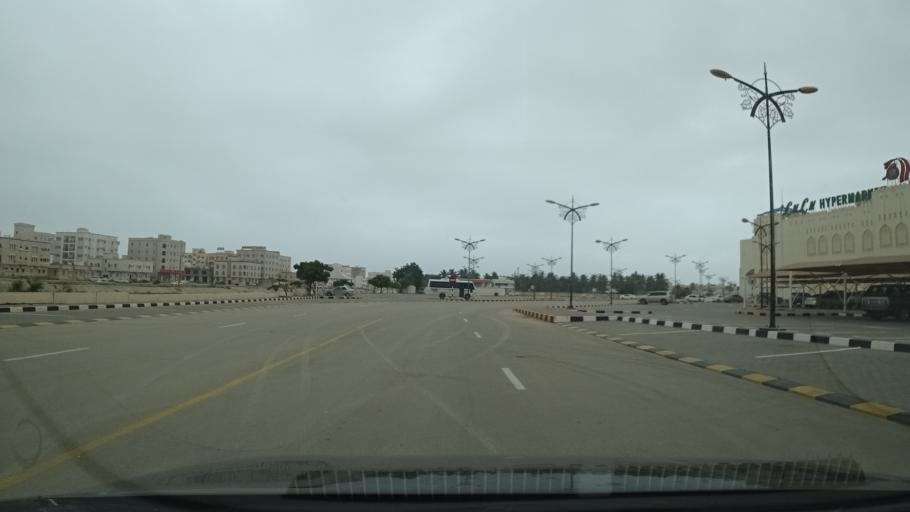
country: OM
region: Zufar
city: Salalah
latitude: 17.0178
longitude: 54.0627
